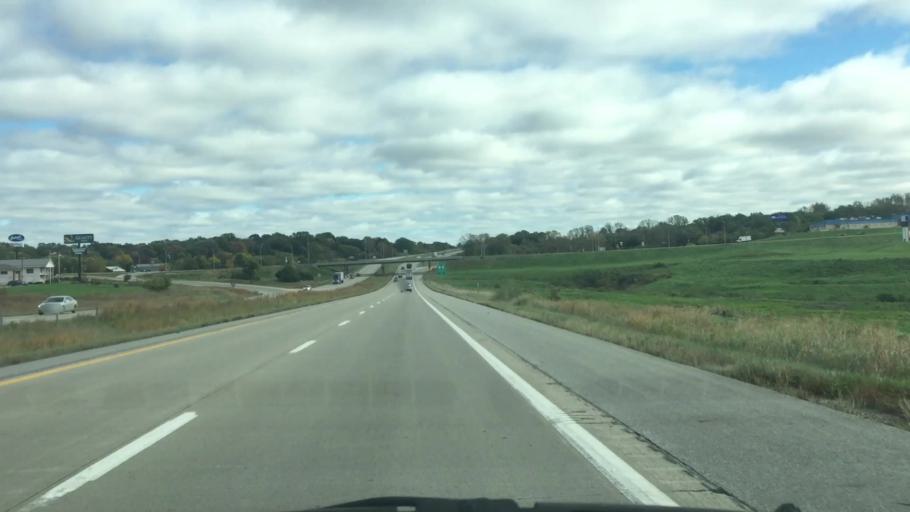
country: US
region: Iowa
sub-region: Jasper County
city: Newton
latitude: 41.6827
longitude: -93.0826
